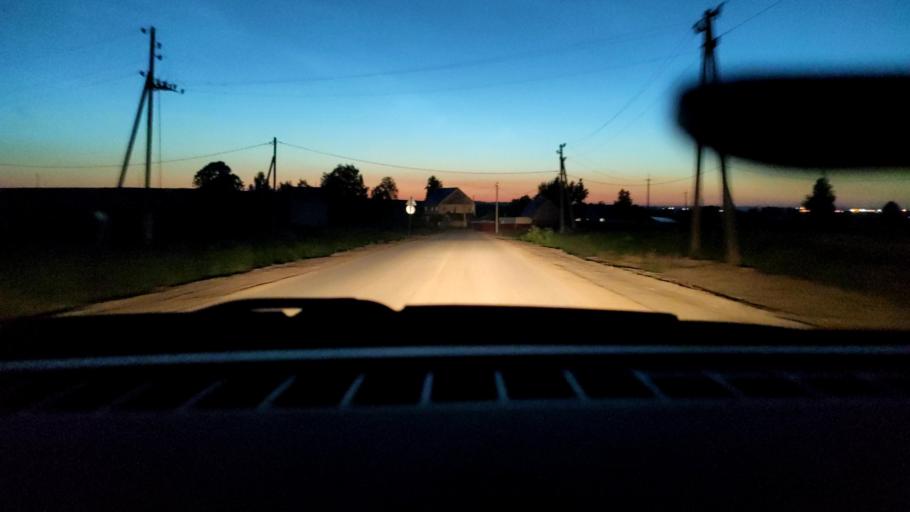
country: RU
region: Perm
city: Kultayevo
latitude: 57.8568
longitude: 55.9832
